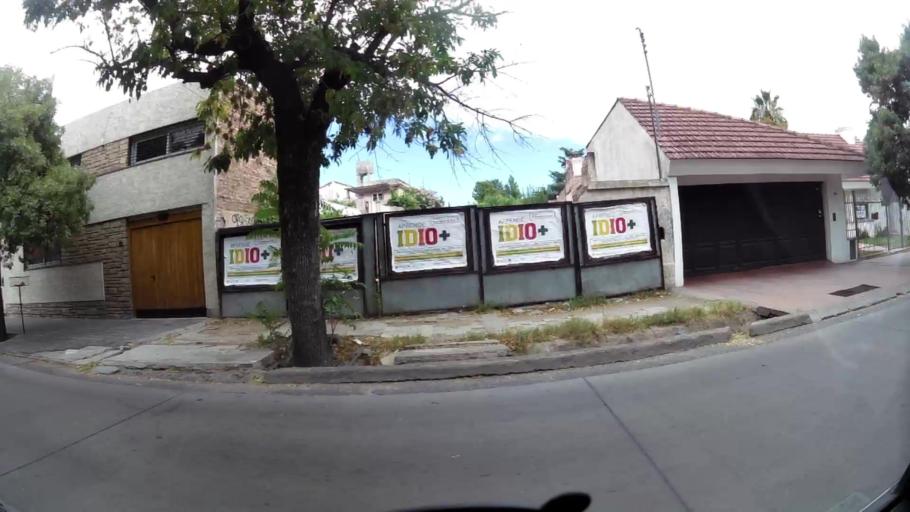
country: AR
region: Mendoza
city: Mendoza
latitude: -32.8854
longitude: -68.8590
